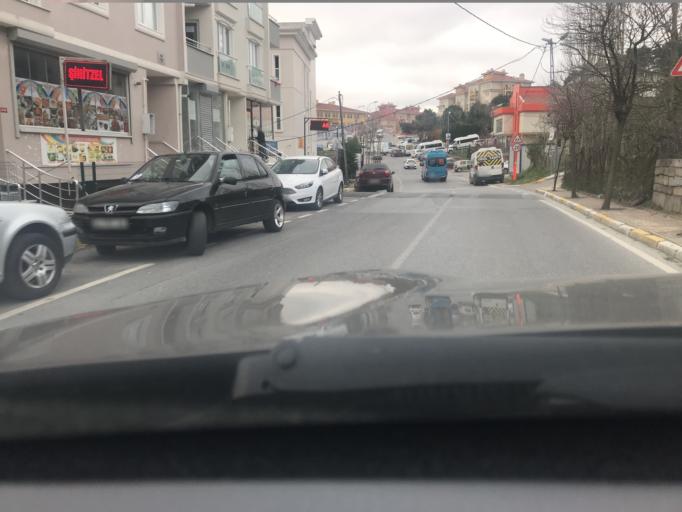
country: TR
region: Istanbul
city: Umraniye
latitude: 41.0364
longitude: 29.1632
